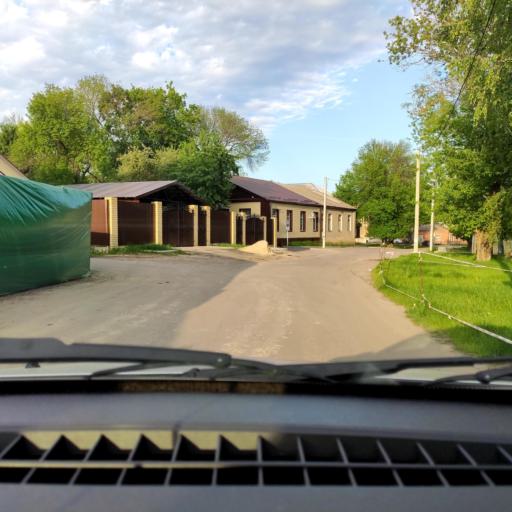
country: RU
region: Voronezj
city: Ramon'
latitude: 51.9149
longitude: 39.3432
